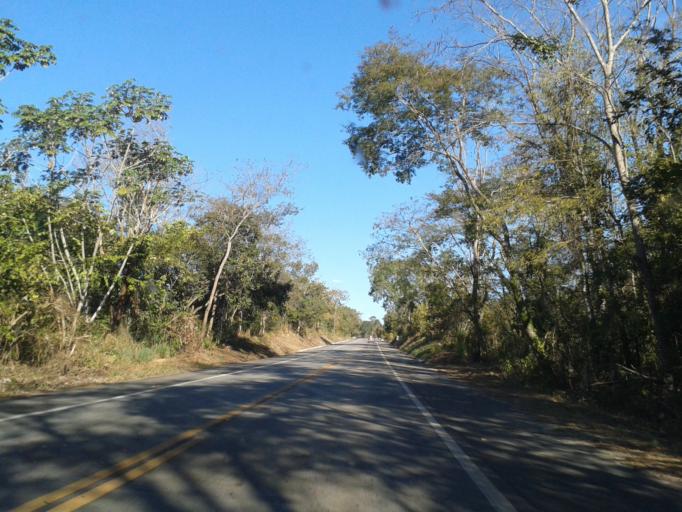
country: BR
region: Goias
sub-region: Itapuranga
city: Itapuranga
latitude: -15.3504
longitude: -50.4064
